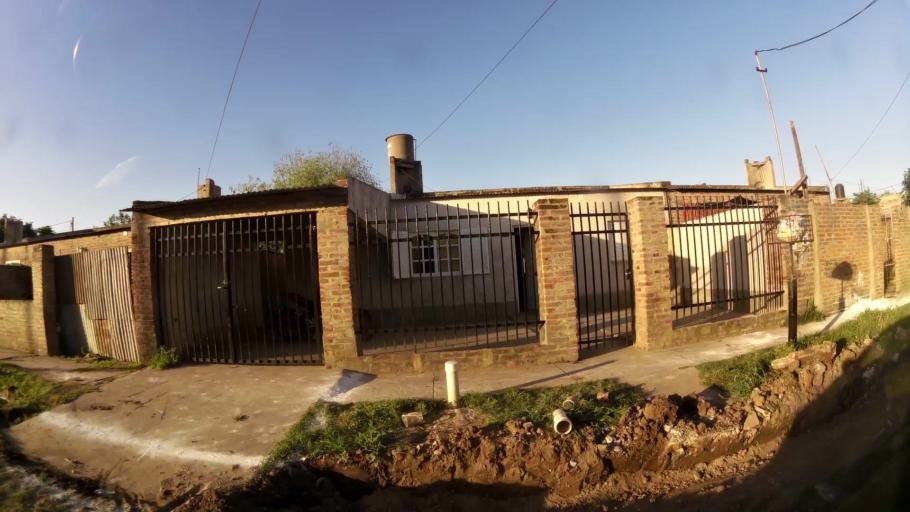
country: AR
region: Santa Fe
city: Santa Fe de la Vera Cruz
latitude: -31.5955
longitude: -60.6849
